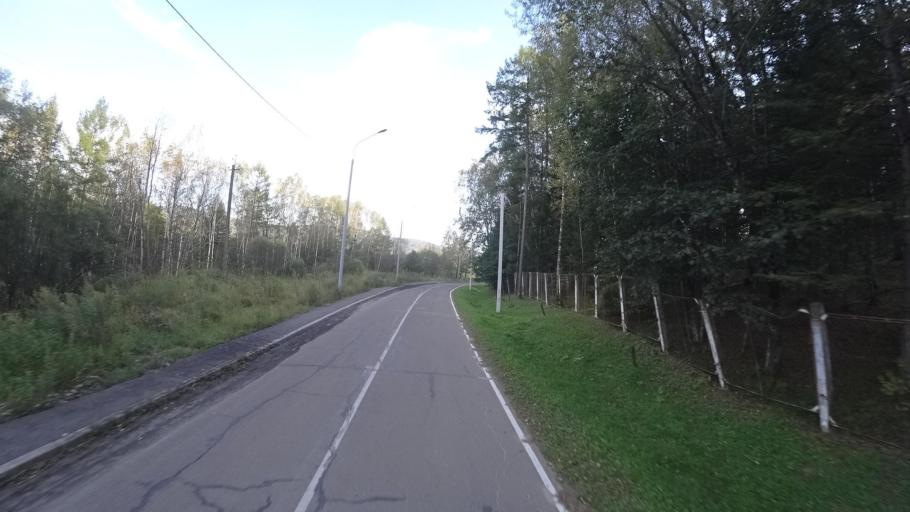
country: RU
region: Jewish Autonomous Oblast
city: Kul'dur
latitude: 49.2100
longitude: 131.6218
